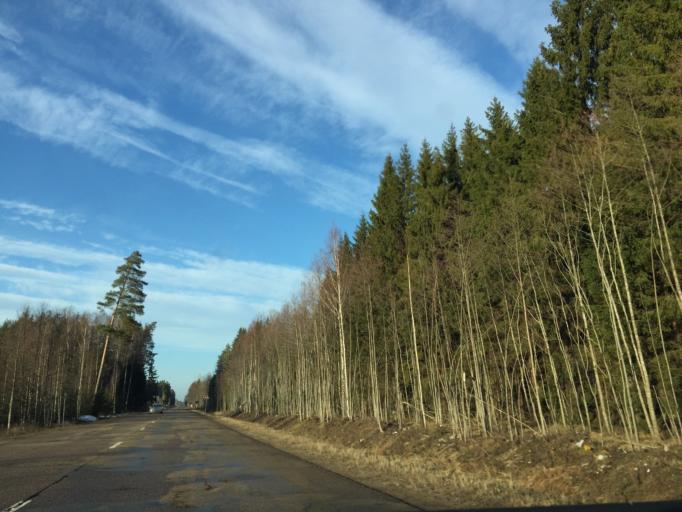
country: LV
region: Lecava
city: Iecava
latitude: 56.7022
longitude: 24.1139
